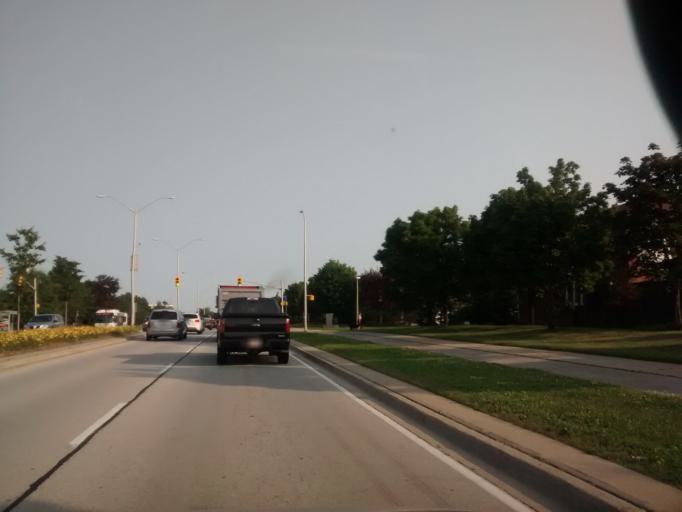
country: CA
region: Ontario
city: Oakville
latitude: 43.4315
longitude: -79.7347
